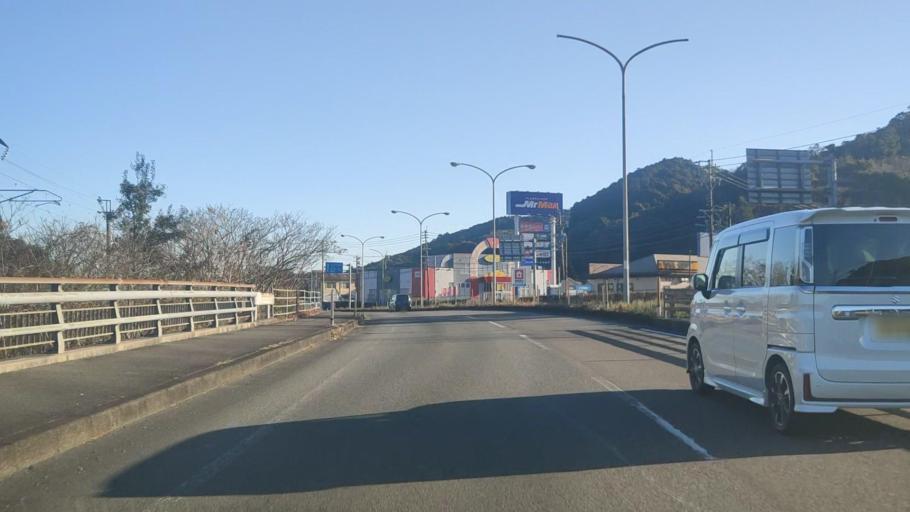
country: JP
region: Miyazaki
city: Nobeoka
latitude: 32.4495
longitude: 131.6385
